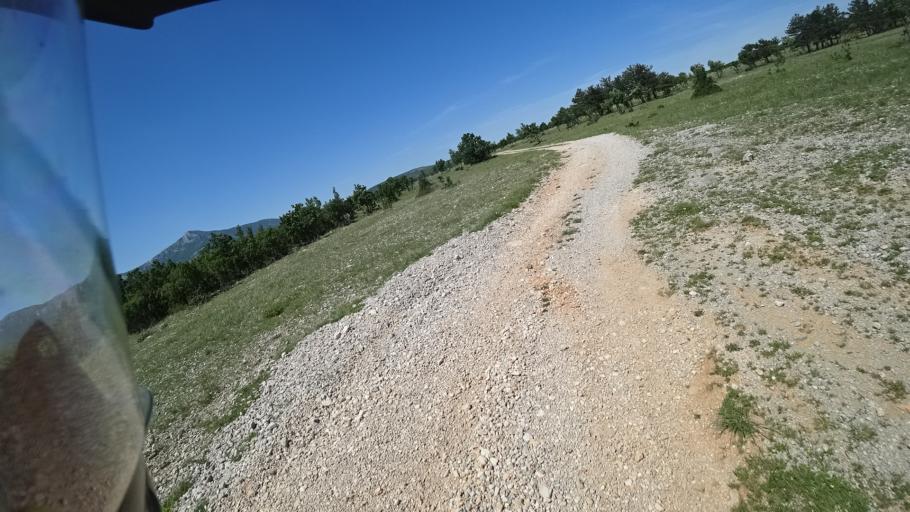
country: BA
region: Federation of Bosnia and Herzegovina
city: Bosansko Grahovo
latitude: 44.0046
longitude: 16.3908
